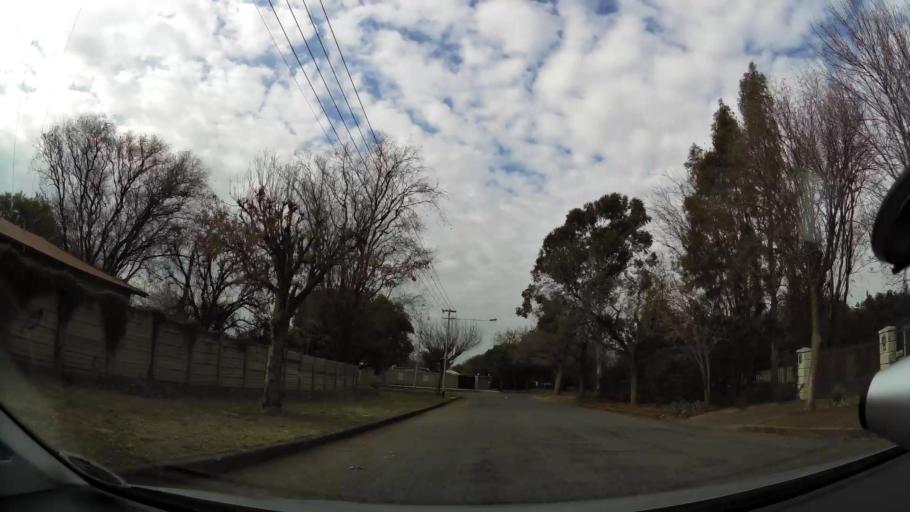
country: ZA
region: Orange Free State
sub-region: Mangaung Metropolitan Municipality
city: Bloemfontein
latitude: -29.0851
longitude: 26.2540
